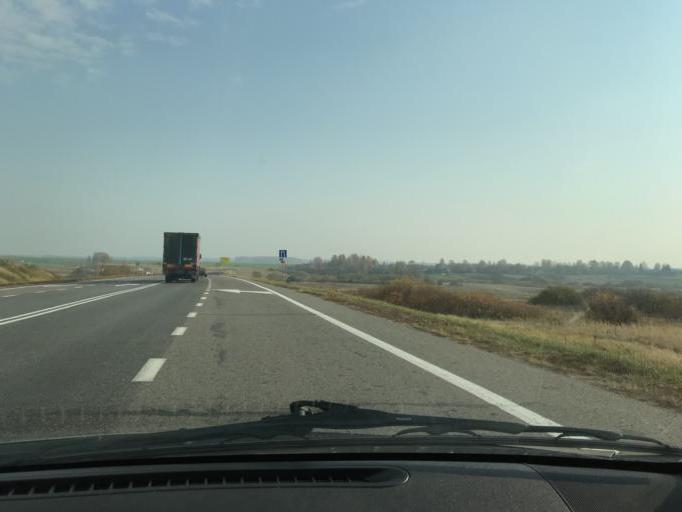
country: BY
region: Vitebsk
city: Chashniki
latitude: 55.0064
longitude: 29.1444
